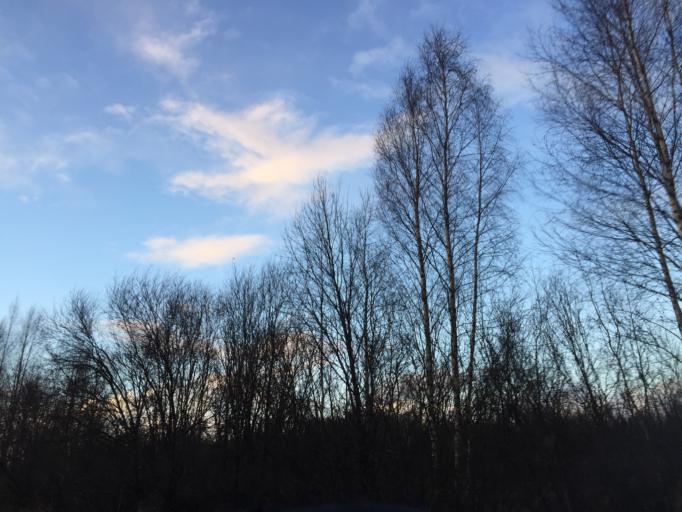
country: LV
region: Burtnieki
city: Matisi
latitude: 57.6785
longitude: 25.2005
